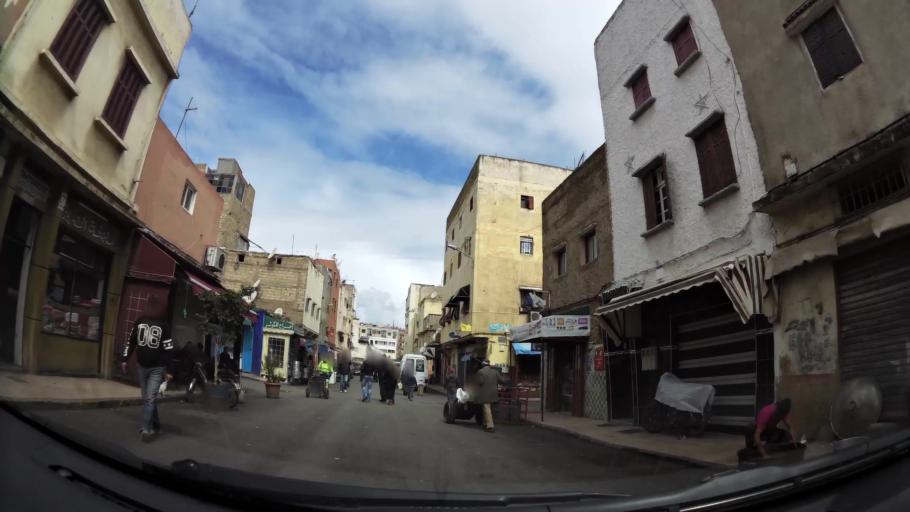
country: MA
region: Grand Casablanca
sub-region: Casablanca
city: Casablanca
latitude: 33.5770
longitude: -7.6317
